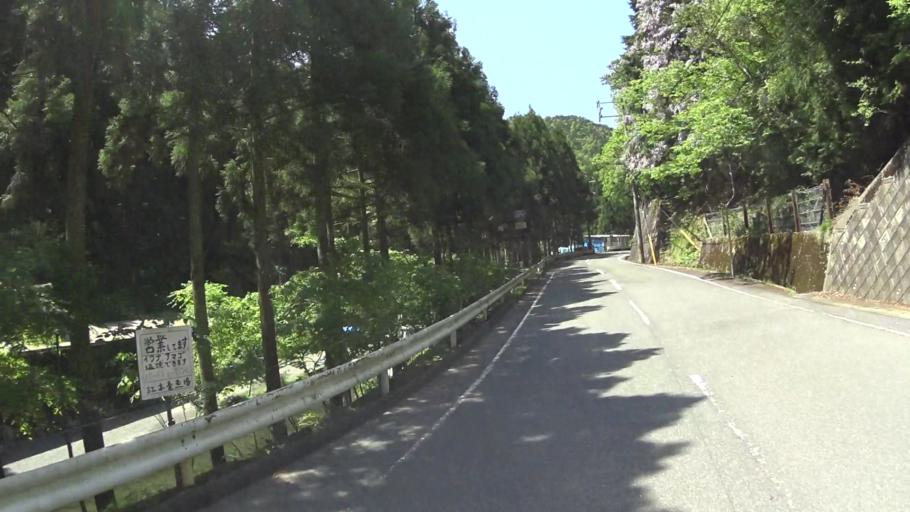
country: JP
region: Shiga Prefecture
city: Kitahama
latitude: 35.1510
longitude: 135.8196
